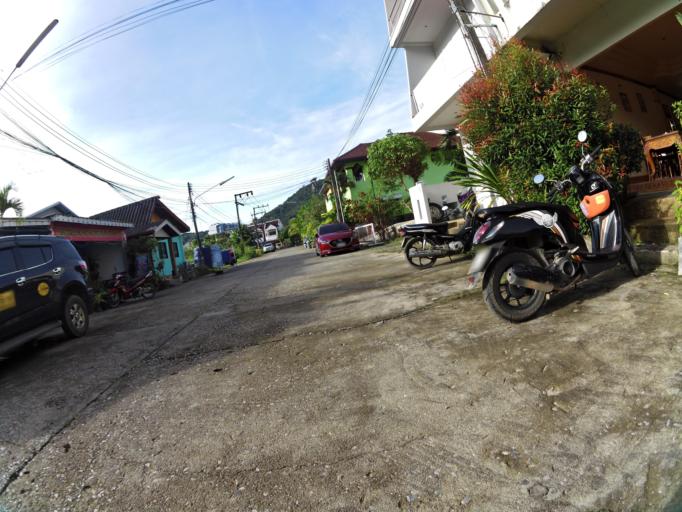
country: TH
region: Phuket
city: Patong
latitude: 7.9500
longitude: 98.2816
